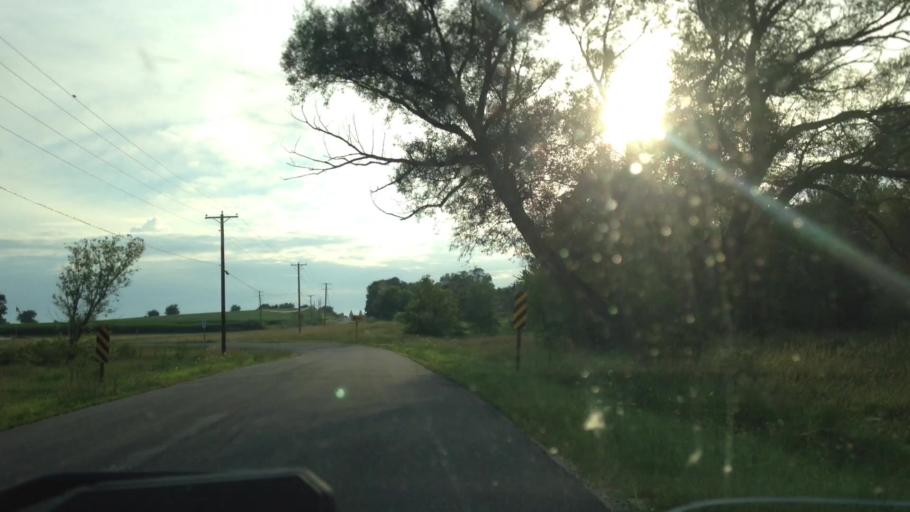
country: US
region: Wisconsin
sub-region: Dodge County
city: Mayville
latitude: 43.4933
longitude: -88.5189
